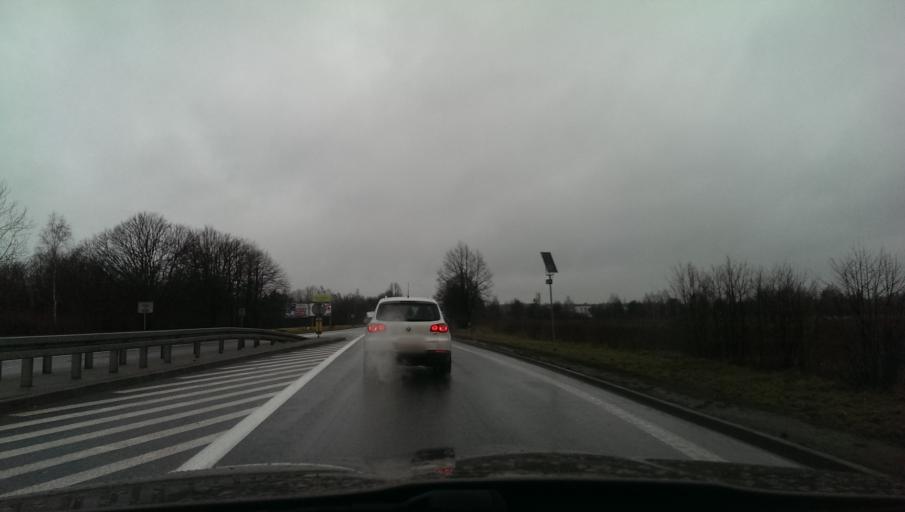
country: PL
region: Subcarpathian Voivodeship
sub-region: Powiat rzeszowski
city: Rudna Mala
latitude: 50.1093
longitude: 21.9752
